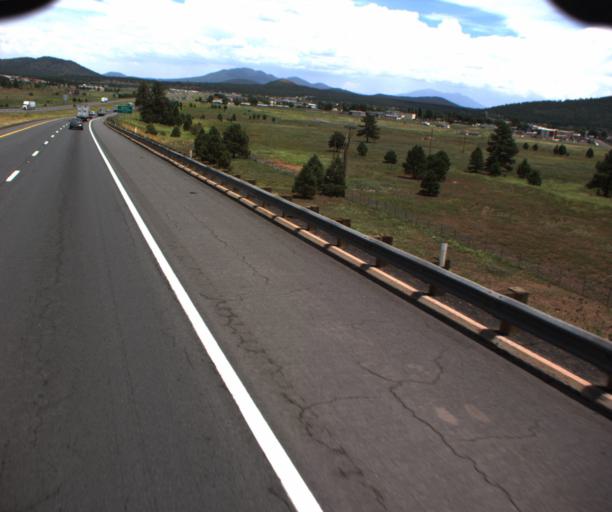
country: US
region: Arizona
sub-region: Coconino County
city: Williams
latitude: 35.2510
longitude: -112.2072
